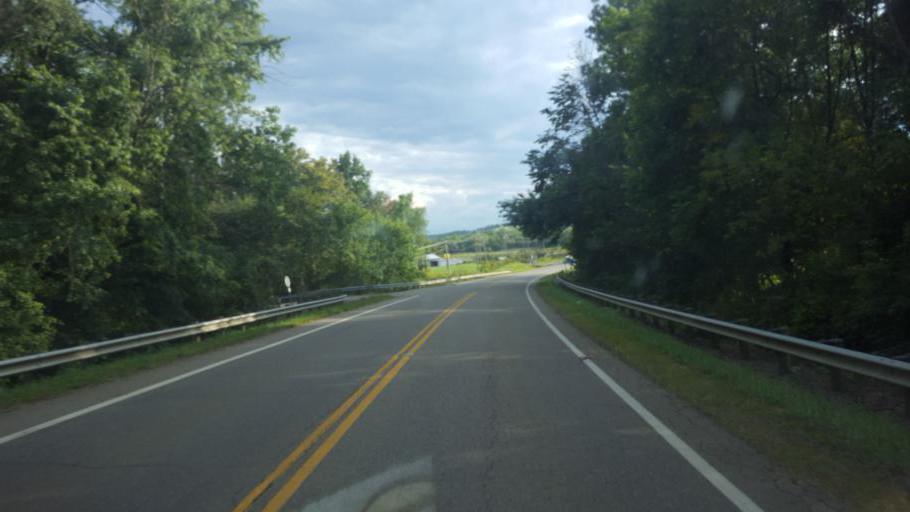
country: US
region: Ohio
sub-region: Holmes County
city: Millersburg
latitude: 40.4869
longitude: -81.9801
